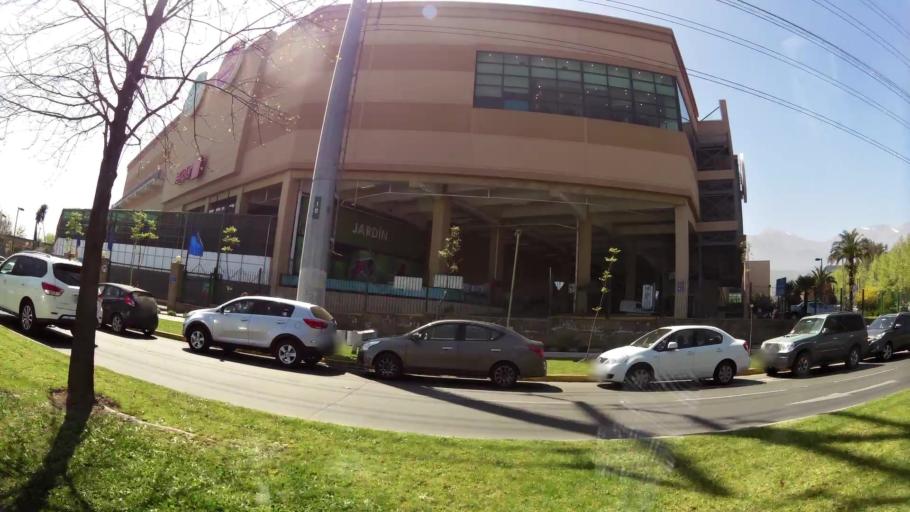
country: CL
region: Santiago Metropolitan
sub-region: Provincia de Santiago
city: Villa Presidente Frei, Nunoa, Santiago, Chile
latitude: -33.4286
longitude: -70.5419
